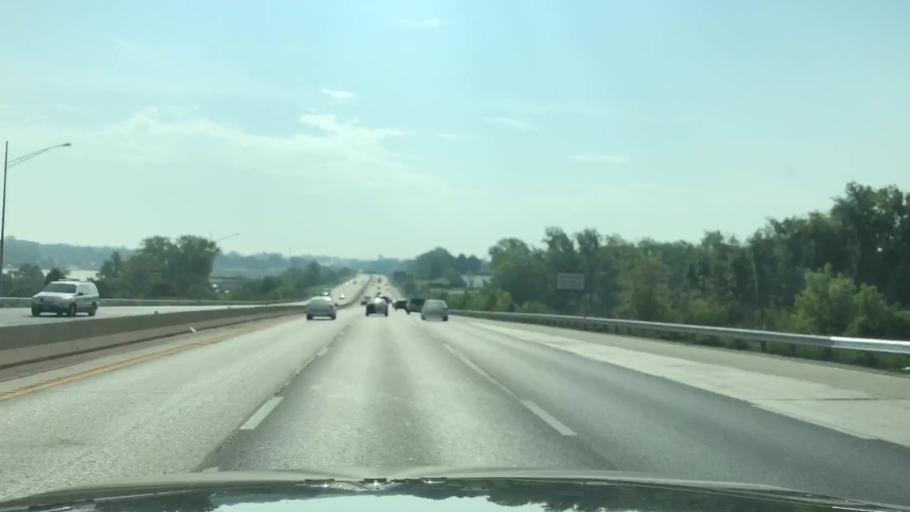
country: US
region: Missouri
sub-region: Saint Louis County
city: Bridgeton
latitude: 38.7459
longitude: -90.4317
